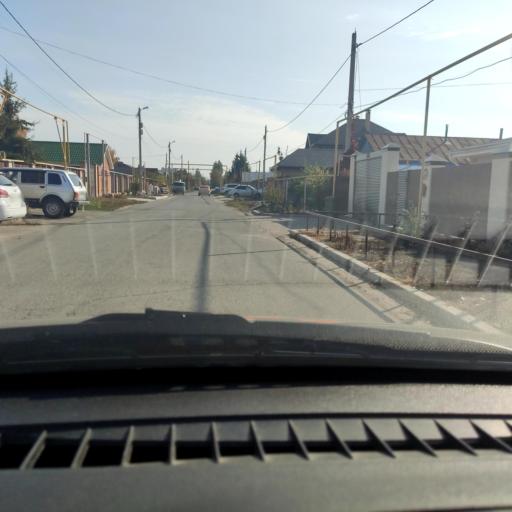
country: RU
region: Samara
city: Podstepki
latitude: 53.5135
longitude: 49.2356
